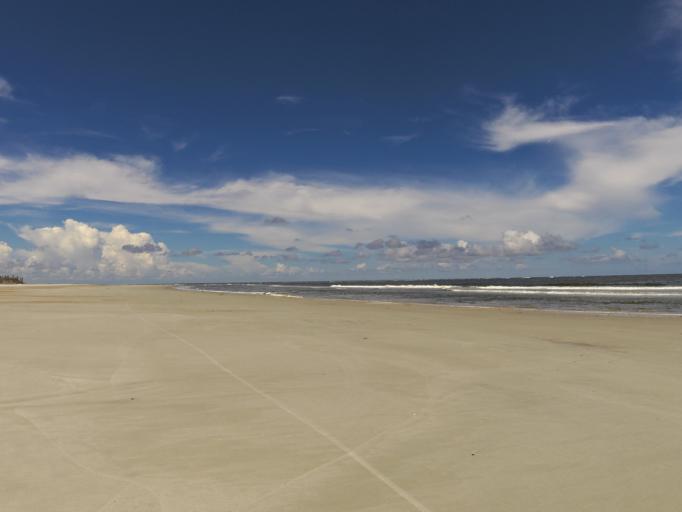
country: US
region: Florida
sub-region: Duval County
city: Atlantic Beach
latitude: 30.4781
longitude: -81.4135
